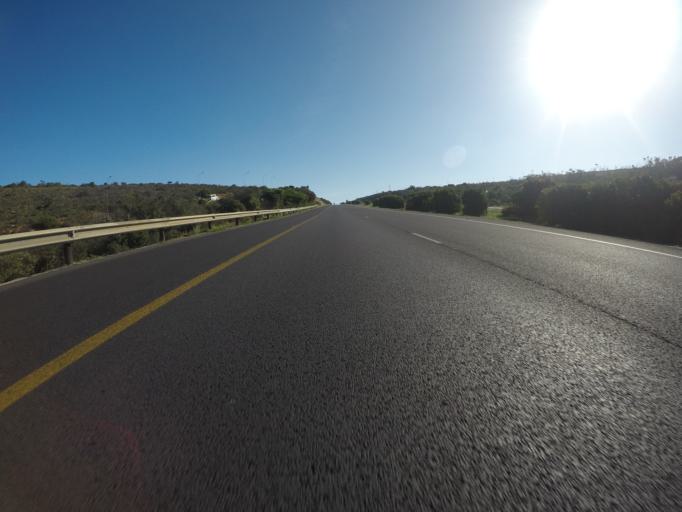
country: ZA
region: Western Cape
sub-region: Eden District Municipality
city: Mossel Bay
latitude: -34.1608
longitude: 22.0970
